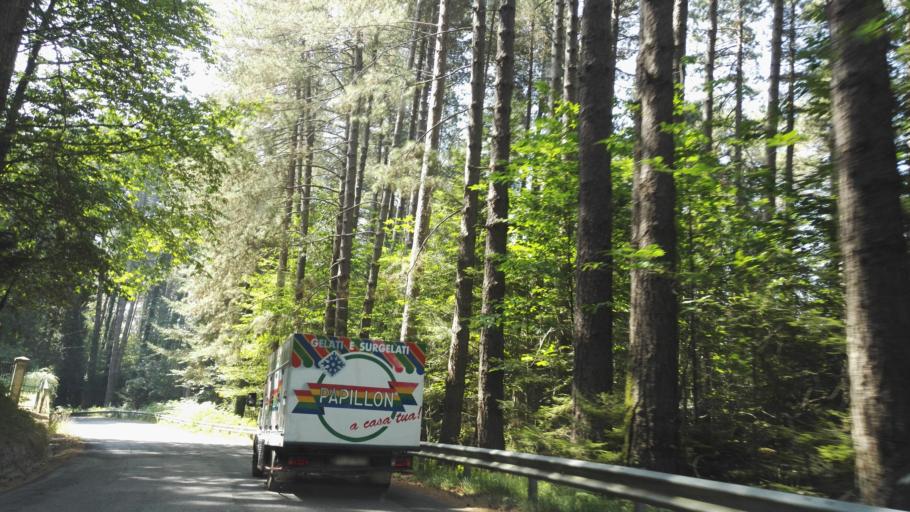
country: IT
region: Calabria
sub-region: Provincia di Vibo-Valentia
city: Mongiana
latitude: 38.5201
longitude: 16.3185
